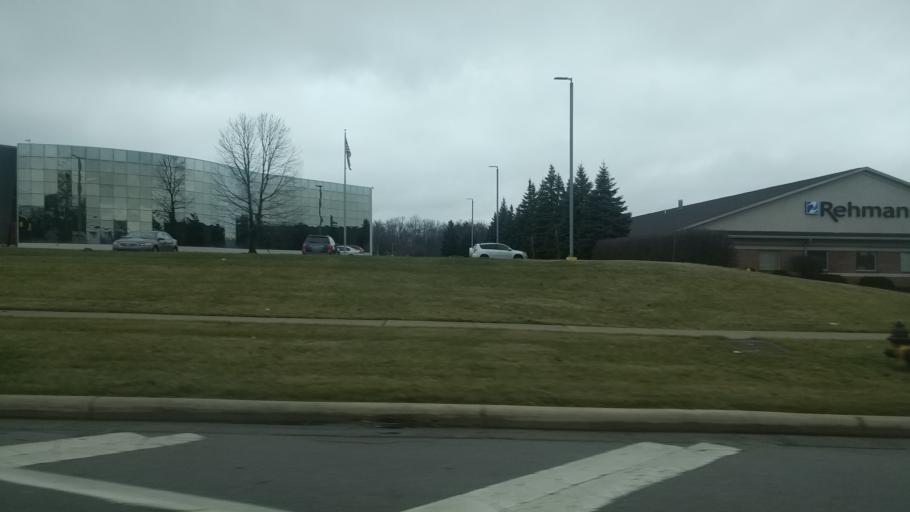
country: US
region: Ohio
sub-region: Lucas County
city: Sylvania
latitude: 41.6737
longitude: -83.7141
